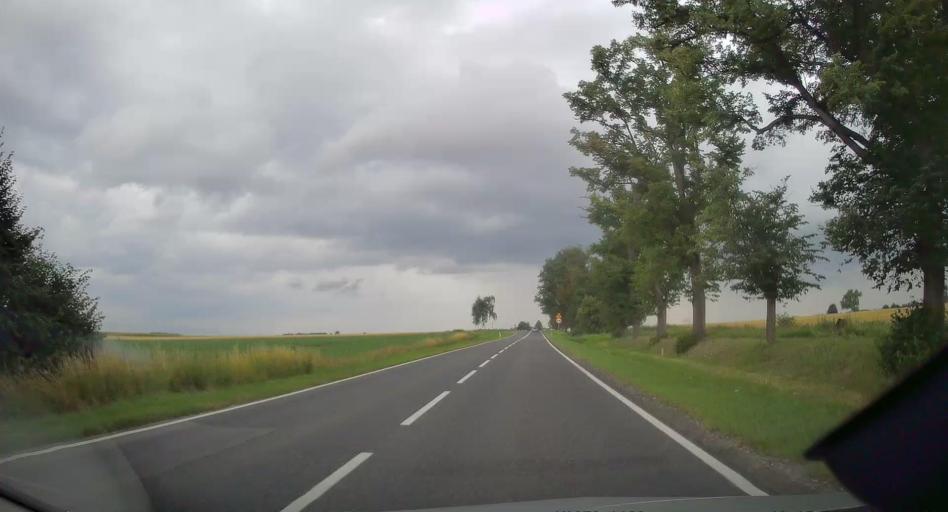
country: PL
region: Opole Voivodeship
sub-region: Powiat prudnicki
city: Laka Prudnicka
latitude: 50.4168
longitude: 17.4860
